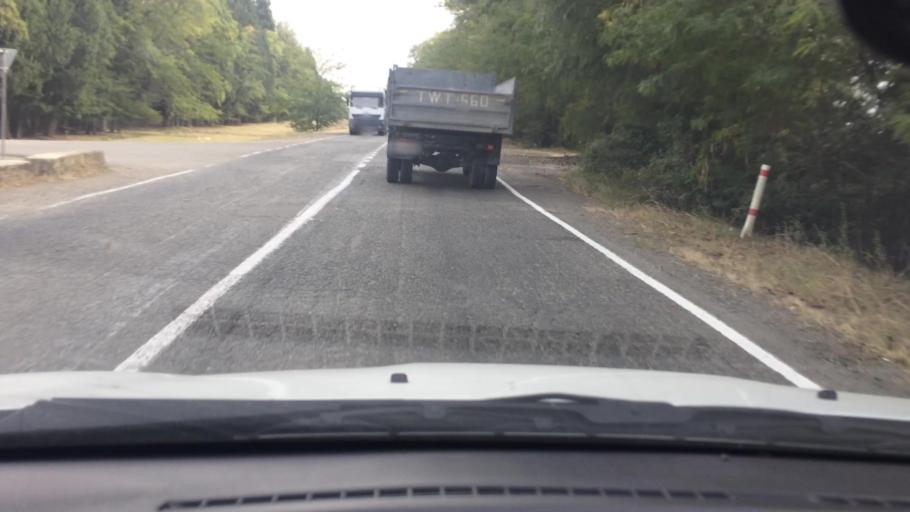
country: GE
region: Kvemo Kartli
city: Rust'avi
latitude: 41.4700
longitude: 44.9797
